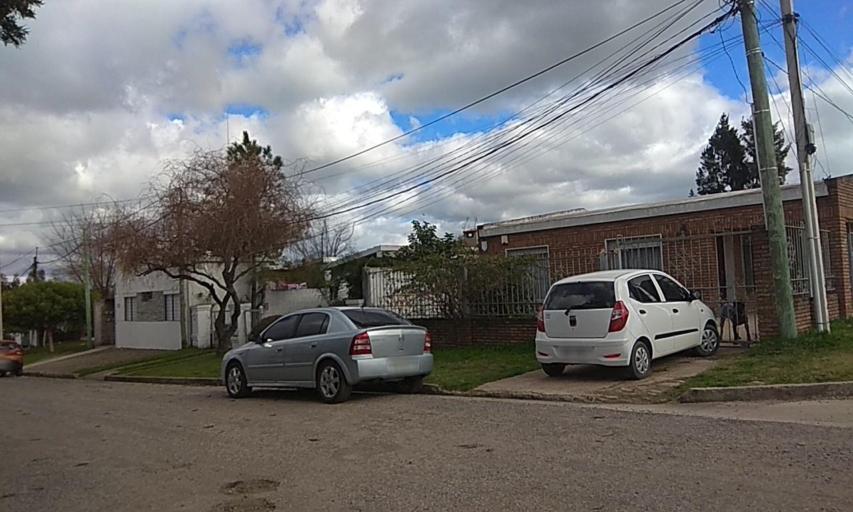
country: UY
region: Florida
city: Florida
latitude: -34.0912
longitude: -56.2325
